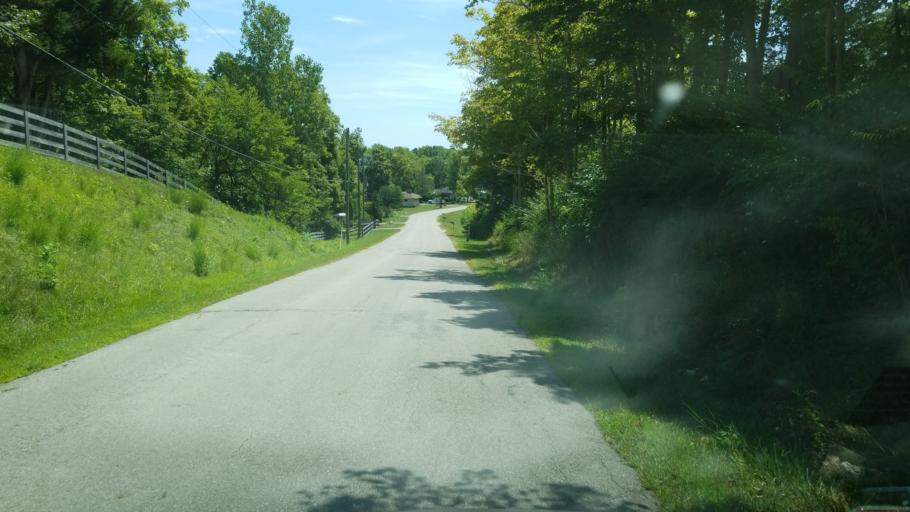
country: US
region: Ohio
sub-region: Franklin County
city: Grove City
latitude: 39.8524
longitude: -83.1932
